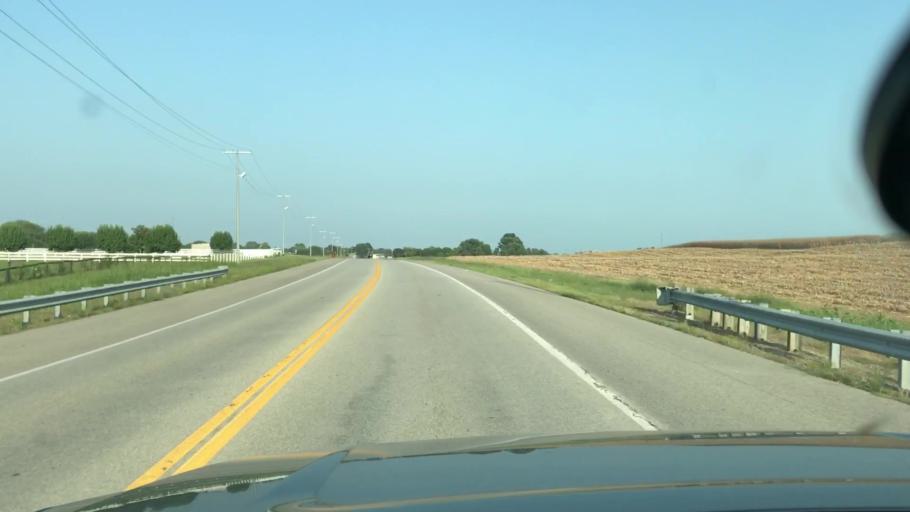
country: US
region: Tennessee
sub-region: Sumner County
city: Portland
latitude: 36.5838
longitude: -86.5805
